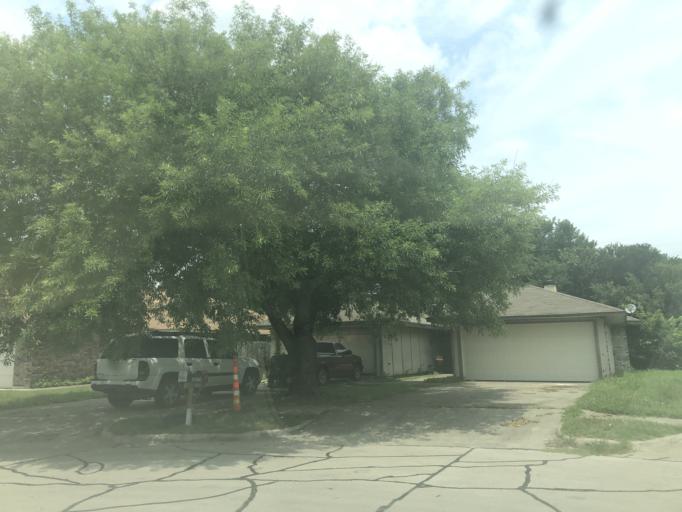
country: US
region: Texas
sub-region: Dallas County
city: Irving
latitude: 32.7967
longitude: -96.9334
